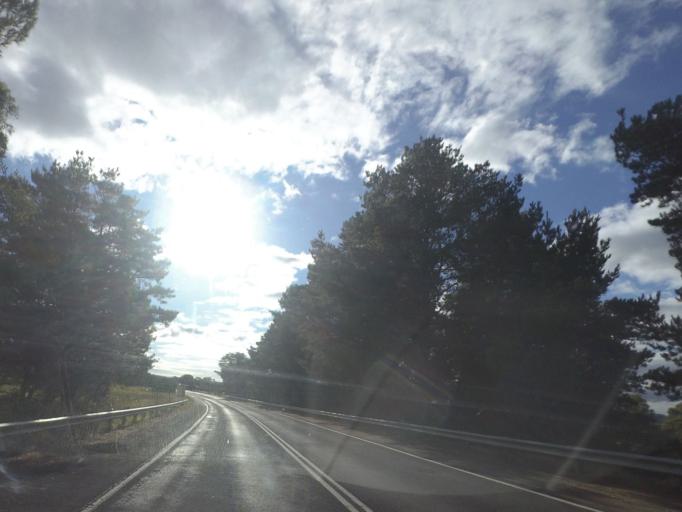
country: AU
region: Victoria
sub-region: Mount Alexander
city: Castlemaine
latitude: -37.1021
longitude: 144.3359
